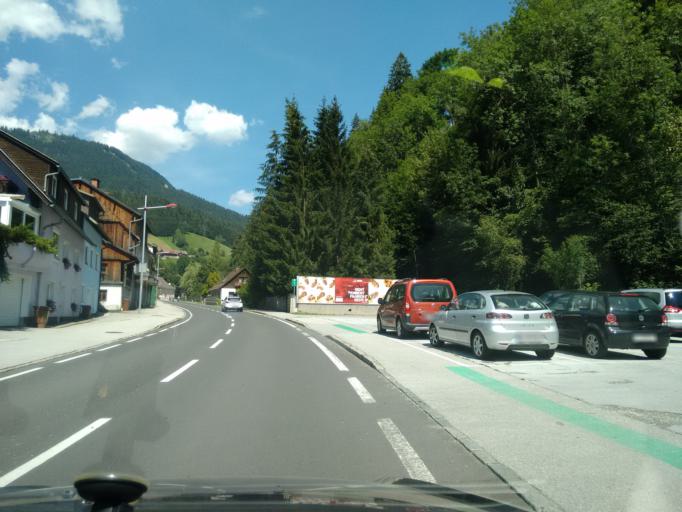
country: AT
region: Styria
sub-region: Politischer Bezirk Liezen
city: Liezen
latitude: 47.5699
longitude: 14.2442
